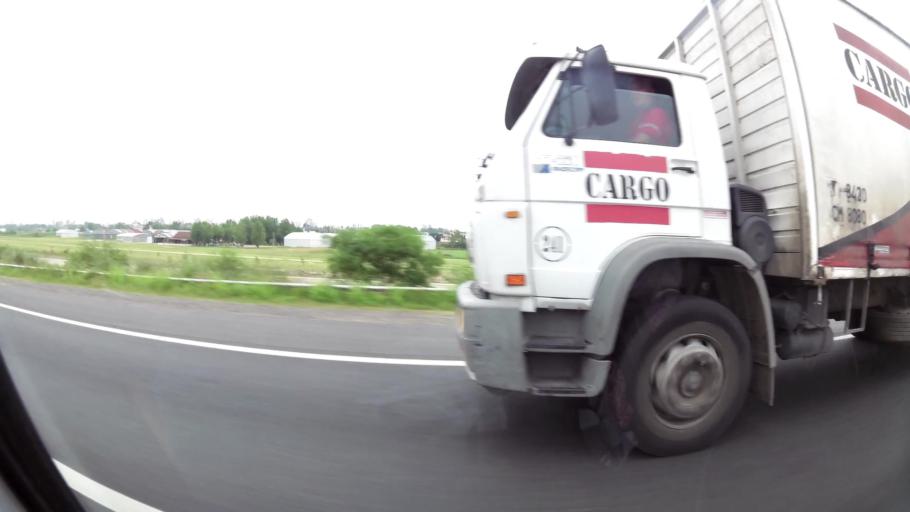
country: AR
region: Buenos Aires
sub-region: Partido de Quilmes
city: Quilmes
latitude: -34.7420
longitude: -58.2058
